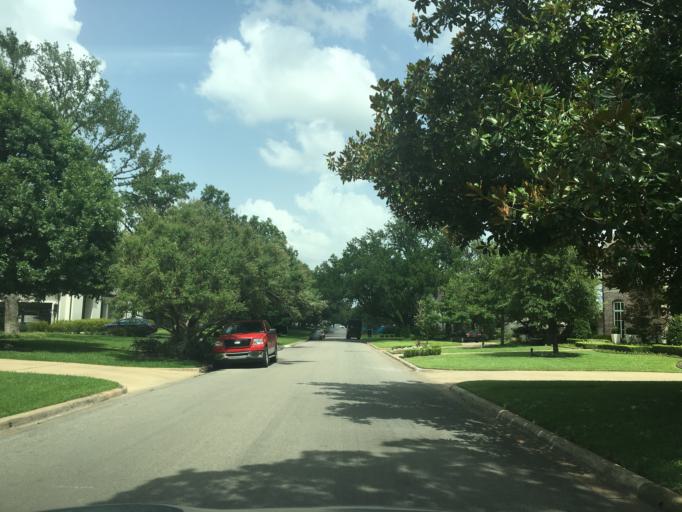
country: US
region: Texas
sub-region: Dallas County
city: University Park
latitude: 32.8904
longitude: -96.7898
